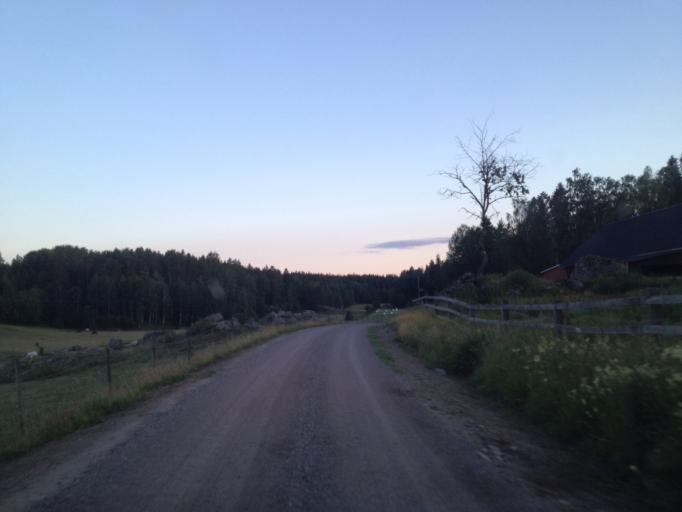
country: SE
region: Kalmar
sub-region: Vasterviks Kommun
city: Overum
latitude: 57.9911
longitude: 16.1781
